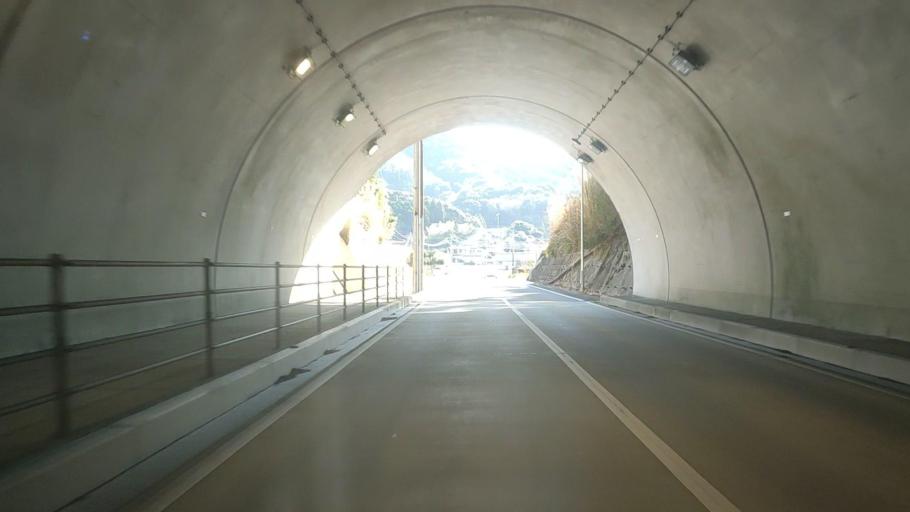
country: JP
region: Oita
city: Saiki
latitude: 32.8042
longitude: 131.8981
